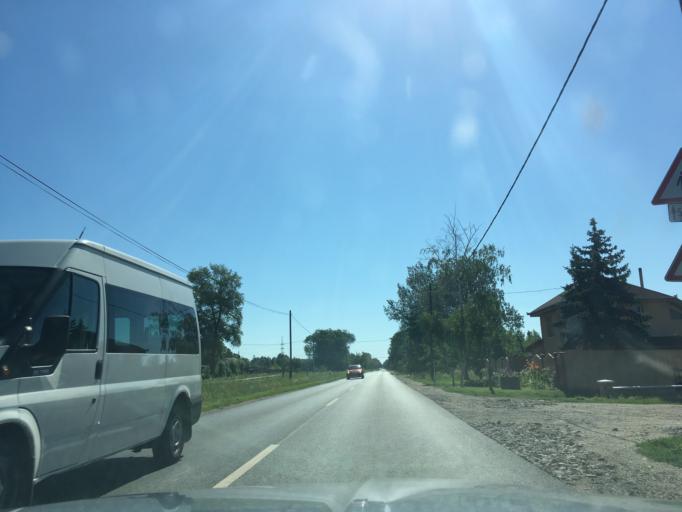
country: HU
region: Hajdu-Bihar
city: Debrecen
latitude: 47.5315
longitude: 21.7005
